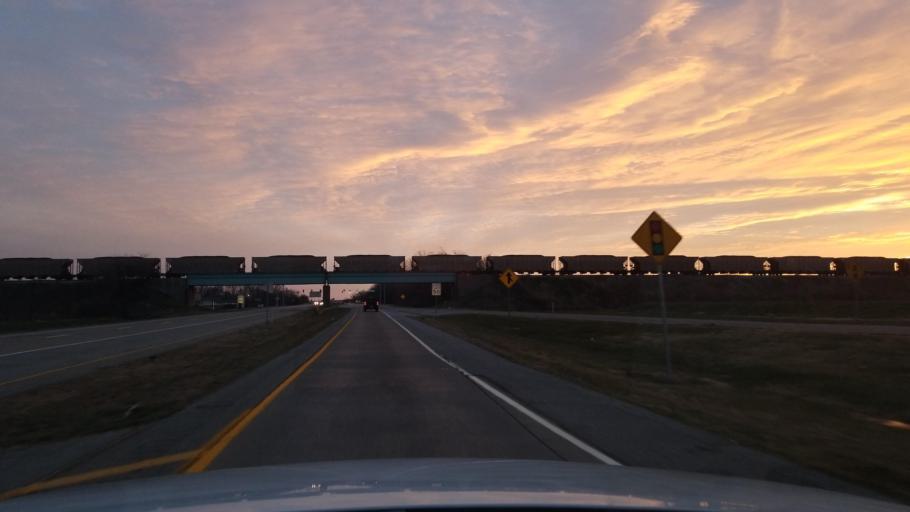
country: US
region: Indiana
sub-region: Posey County
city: Mount Vernon
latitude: 37.9374
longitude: -87.8735
